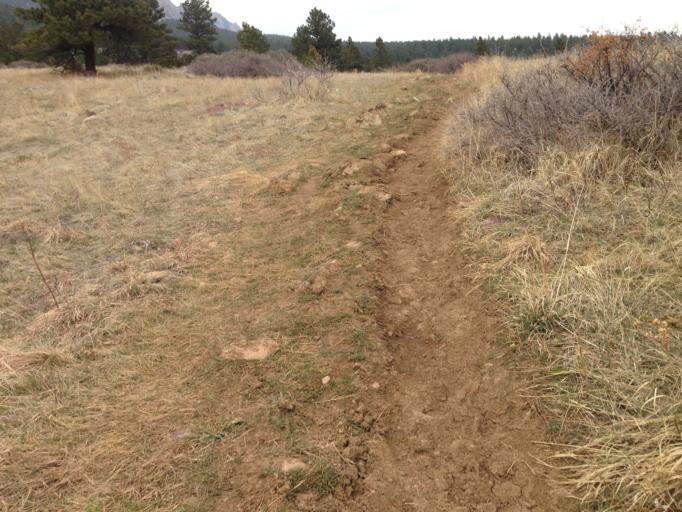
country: US
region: Colorado
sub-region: Boulder County
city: Boulder
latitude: 39.9446
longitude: -105.2711
